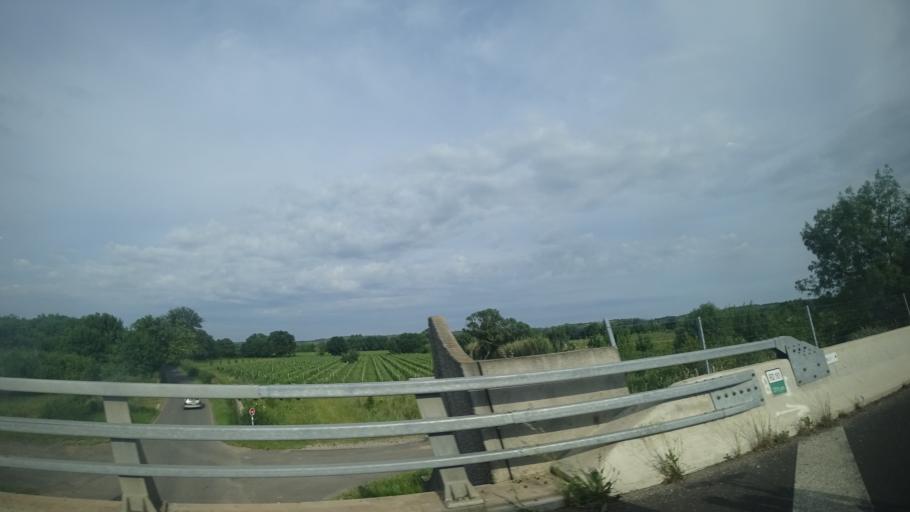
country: FR
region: Languedoc-Roussillon
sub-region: Departement de l'Herault
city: Pezenas
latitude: 43.4651
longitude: 3.4325
